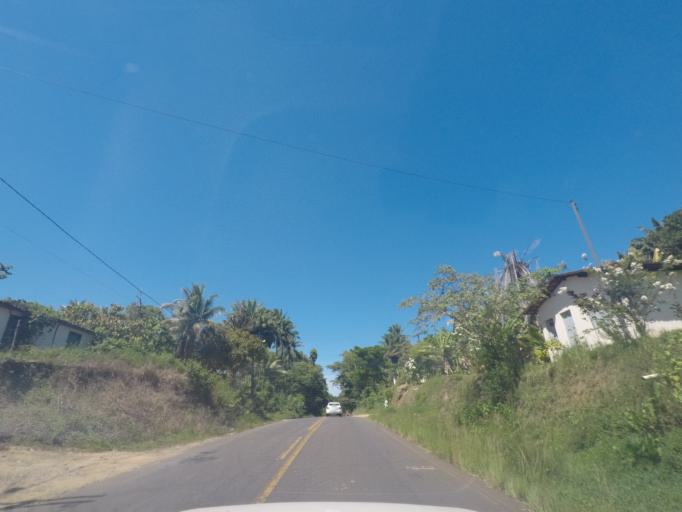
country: BR
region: Bahia
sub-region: Valenca
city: Valenca
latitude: -13.4531
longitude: -39.0868
